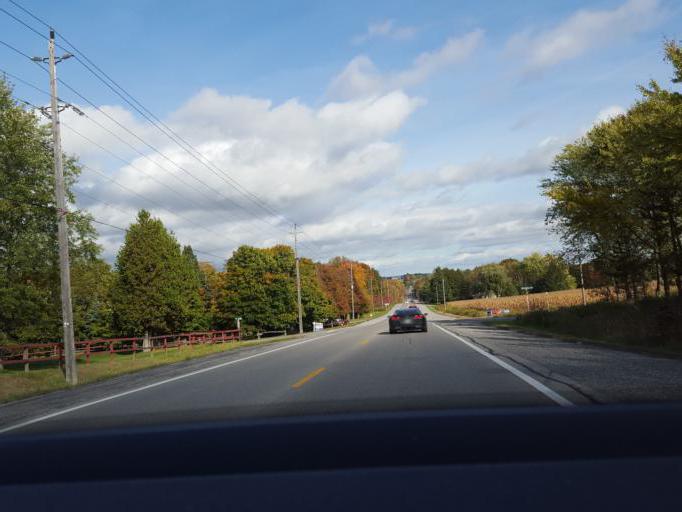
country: CA
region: Ontario
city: Oshawa
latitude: 43.9768
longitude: -78.6894
